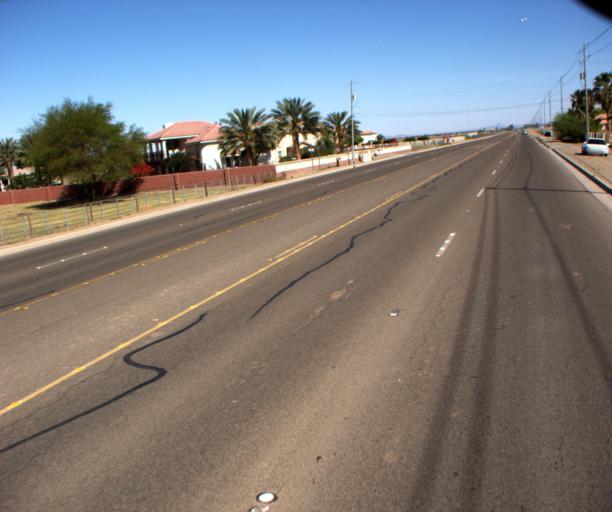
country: US
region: Arizona
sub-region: Yuma County
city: Somerton
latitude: 32.6414
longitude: -114.6500
